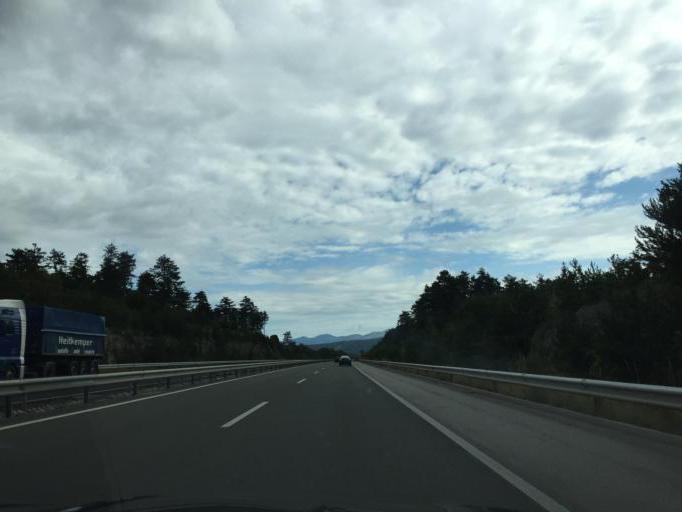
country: SI
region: Divaca
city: Divaca
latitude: 45.6562
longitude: 13.9624
